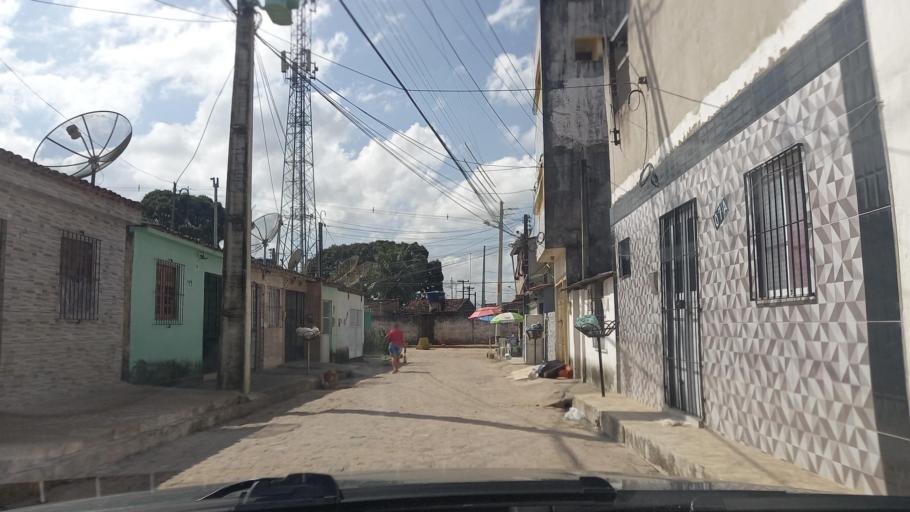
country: BR
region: Pernambuco
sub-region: Goiana
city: Goiana
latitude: -7.5647
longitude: -35.0137
